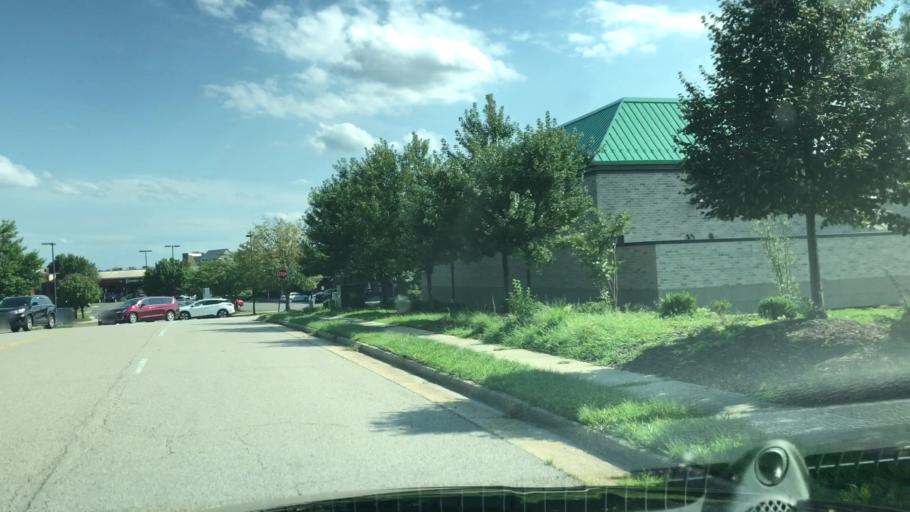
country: US
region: Virginia
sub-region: Prince William County
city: Potomac Mills
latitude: 38.6404
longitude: -77.2959
